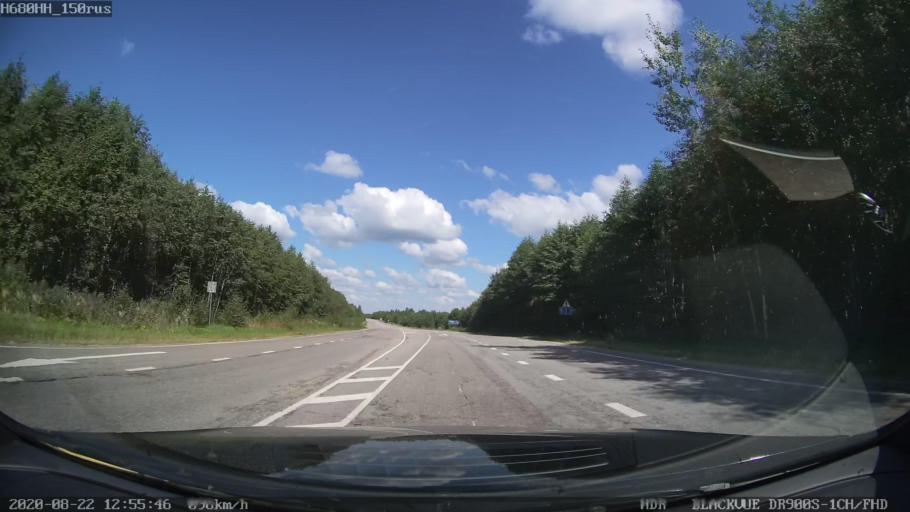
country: RU
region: Tverskaya
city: Rameshki
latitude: 57.5470
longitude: 36.3083
